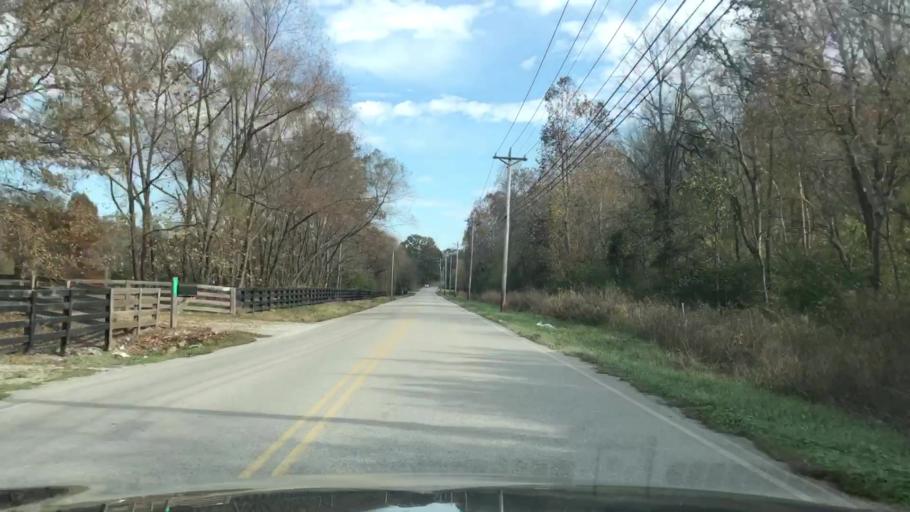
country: US
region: Tennessee
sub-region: Williamson County
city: Franklin
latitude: 35.9143
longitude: -86.8083
